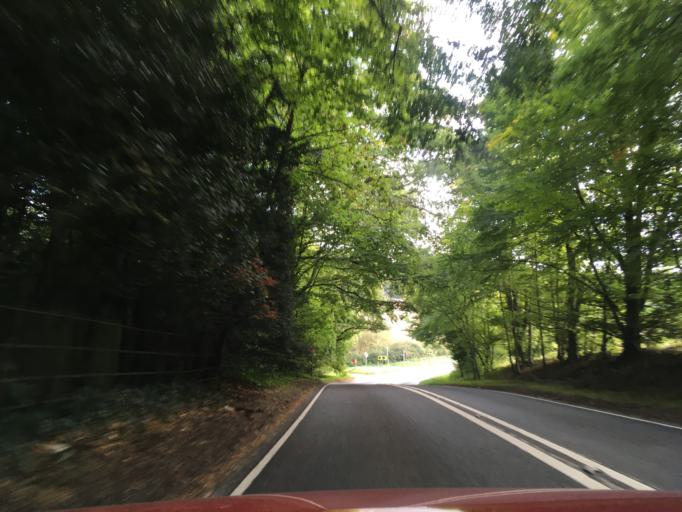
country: GB
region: England
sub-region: Hampshire
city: Basingstoke
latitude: 51.2280
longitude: -1.0638
